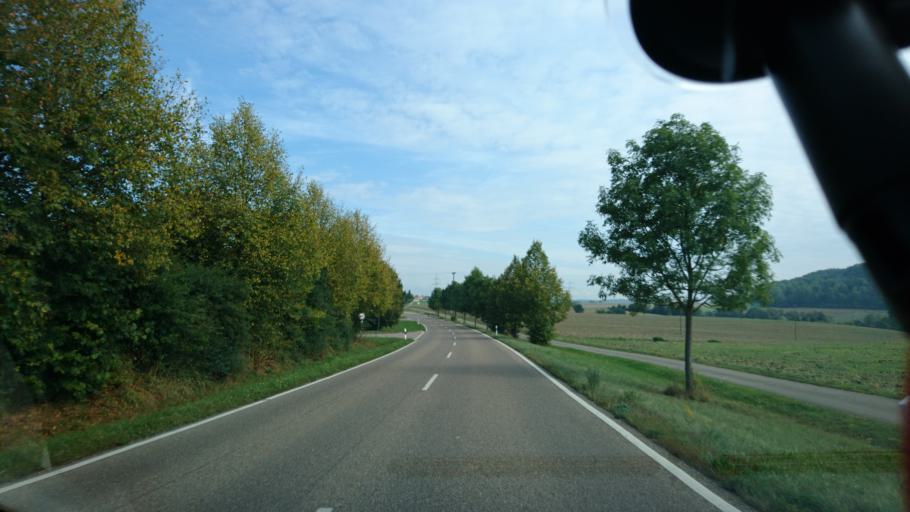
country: DE
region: Baden-Wuerttemberg
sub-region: Regierungsbezirk Stuttgart
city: Vellberg
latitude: 49.1056
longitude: 9.8841
